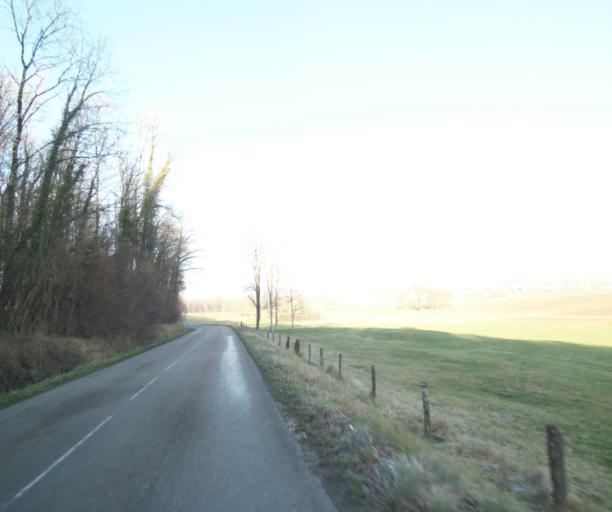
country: FR
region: Champagne-Ardenne
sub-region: Departement de la Haute-Marne
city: Bienville
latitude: 48.5766
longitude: 5.0807
